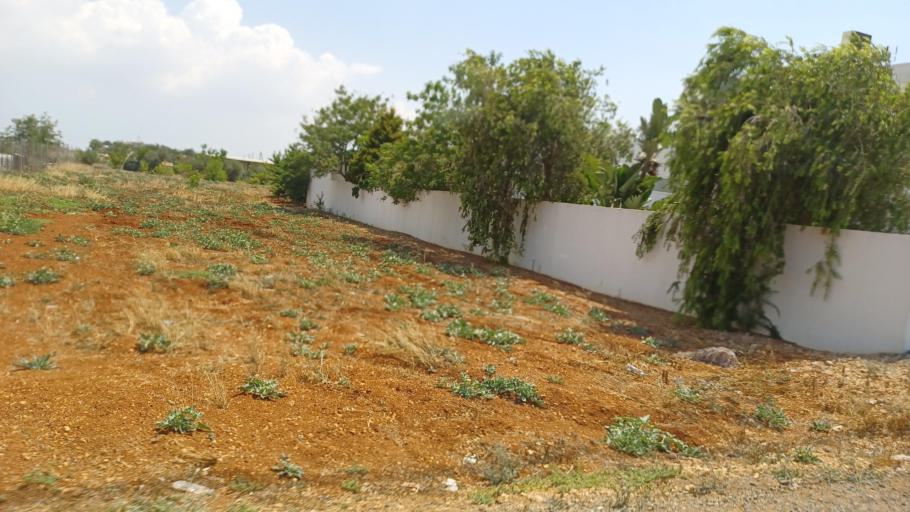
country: CY
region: Ammochostos
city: Liopetri
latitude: 34.9905
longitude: 33.8562
